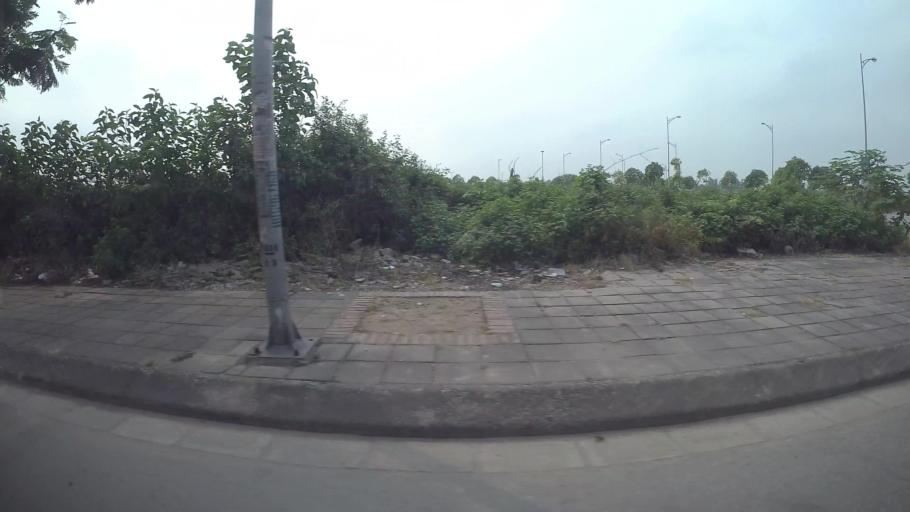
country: VN
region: Ha Noi
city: Hoan Kiem
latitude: 21.0725
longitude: 105.8983
